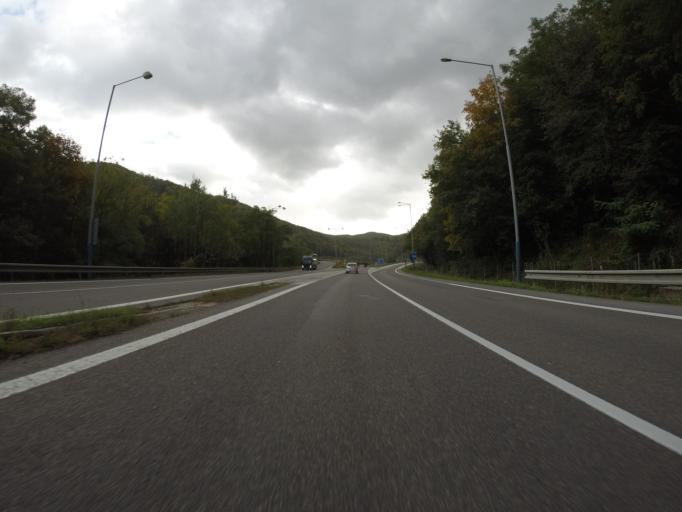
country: SK
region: Banskobystricky
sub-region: Okres Banska Bystrica
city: Zvolen
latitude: 48.5651
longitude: 19.1057
